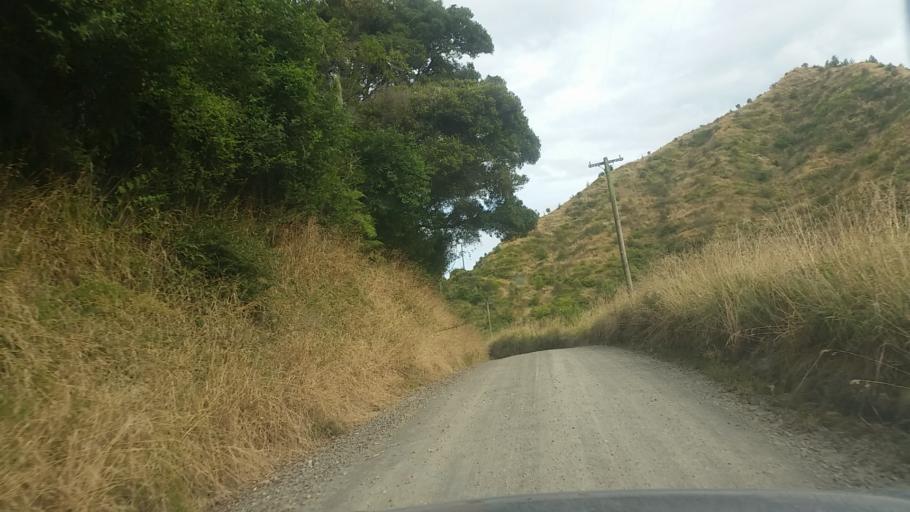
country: NZ
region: Taranaki
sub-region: New Plymouth District
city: Waitara
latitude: -39.1387
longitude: 174.7165
